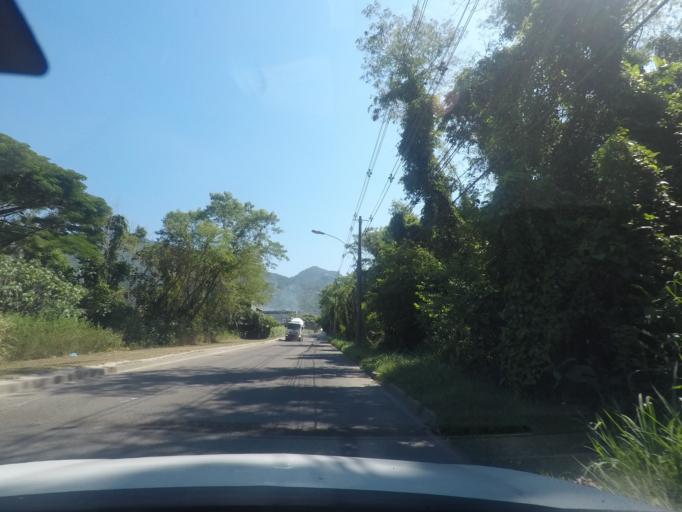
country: BR
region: Rio de Janeiro
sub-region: Nilopolis
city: Nilopolis
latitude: -22.9876
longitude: -43.4536
